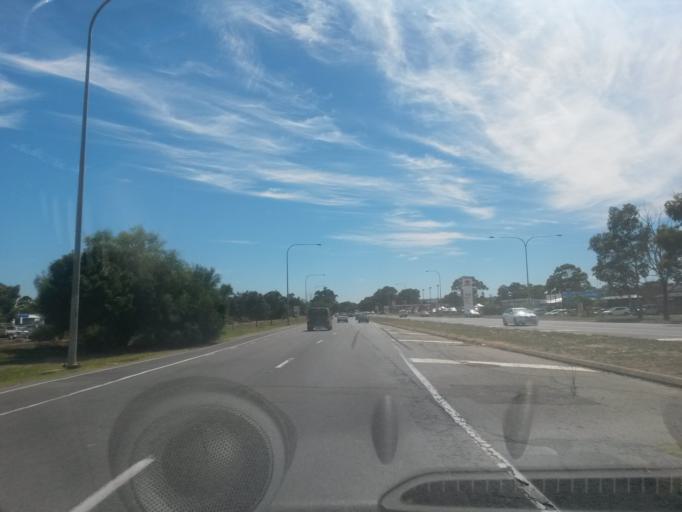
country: AU
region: South Australia
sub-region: Salisbury
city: Salisbury
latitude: -34.7941
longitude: 138.6448
